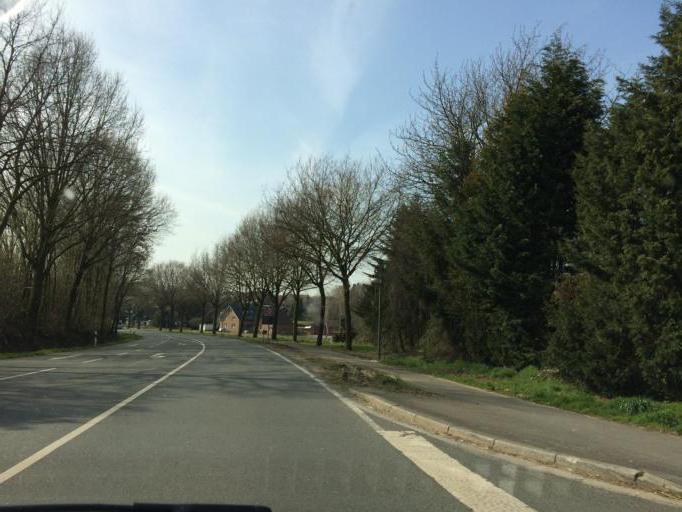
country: DE
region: North Rhine-Westphalia
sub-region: Regierungsbezirk Munster
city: Haltern
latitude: 51.7792
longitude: 7.1596
